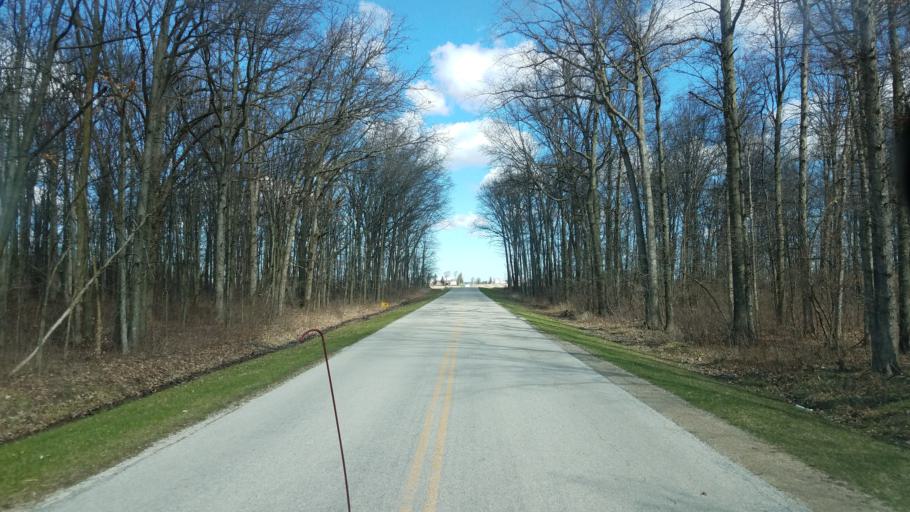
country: US
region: Ohio
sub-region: Sandusky County
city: Mount Carmel
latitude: 41.1832
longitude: -82.9379
